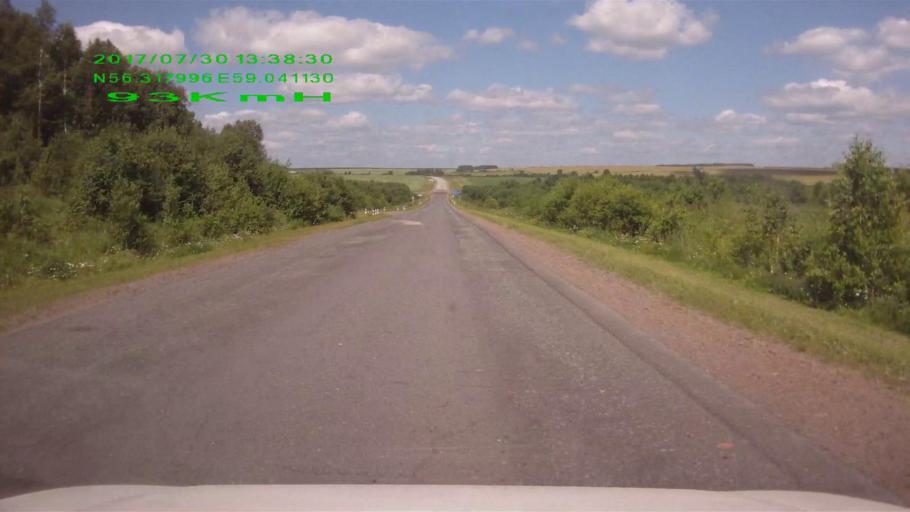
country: RU
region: Sverdlovsk
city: Mikhaylovsk
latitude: 56.3186
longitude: 59.0412
